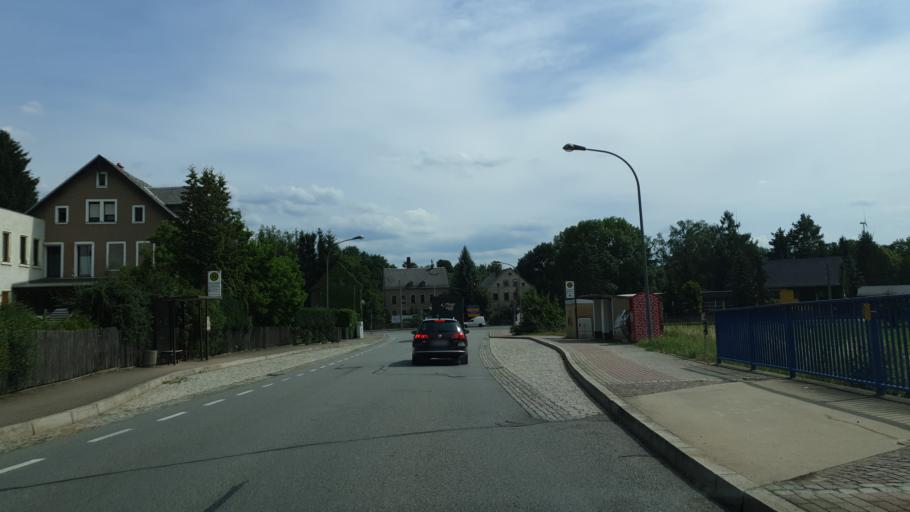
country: DE
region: Saxony
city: Oberlungwitz
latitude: 50.7836
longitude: 12.6933
